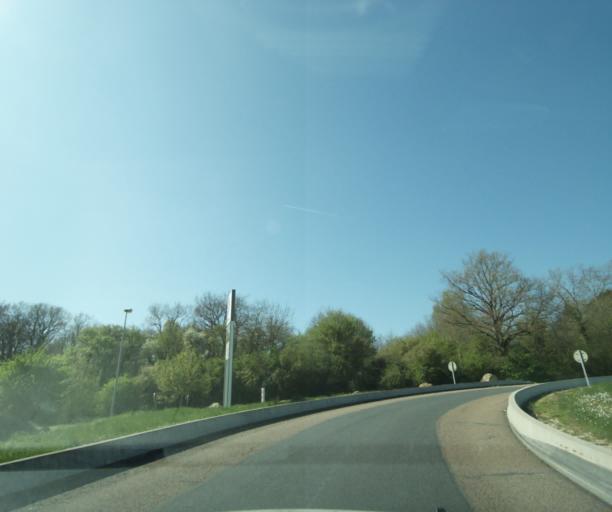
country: FR
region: Bourgogne
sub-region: Departement de la Nievre
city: Pouilly-sur-Loire
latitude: 47.3394
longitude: 2.9277
